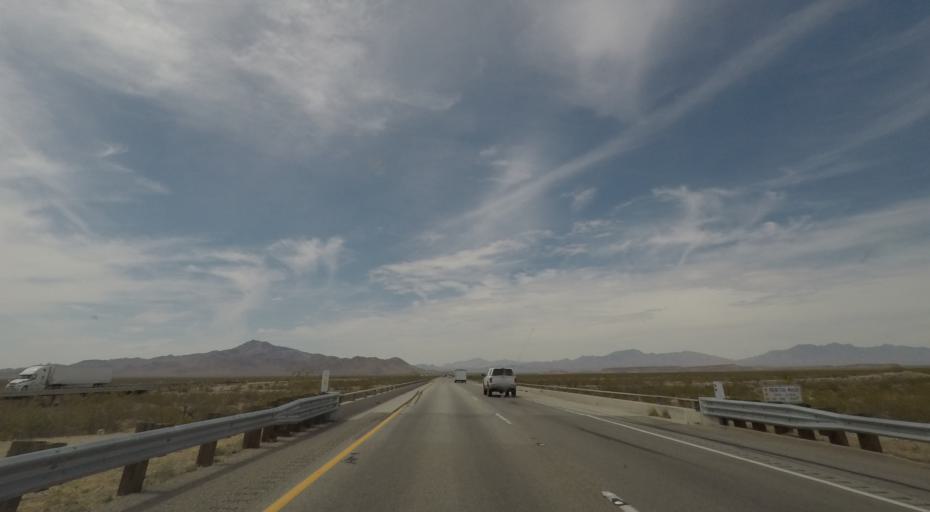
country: US
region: California
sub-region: San Bernardino County
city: Needles
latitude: 34.8066
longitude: -115.2554
